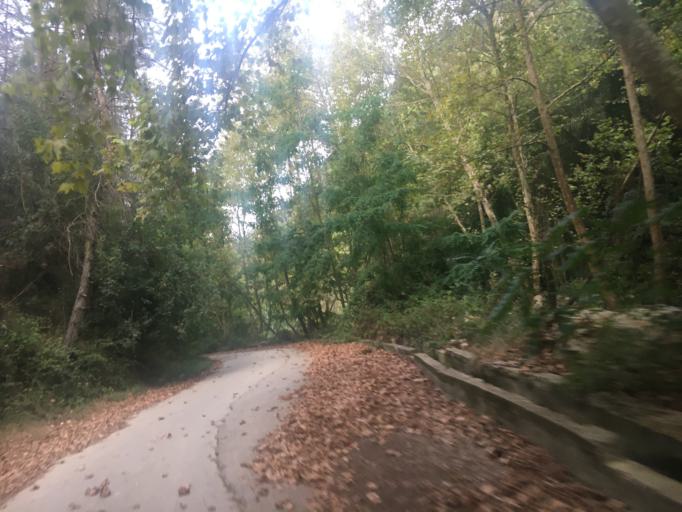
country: LB
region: Mont-Liban
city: Djounie
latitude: 33.9679
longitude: 35.6443
